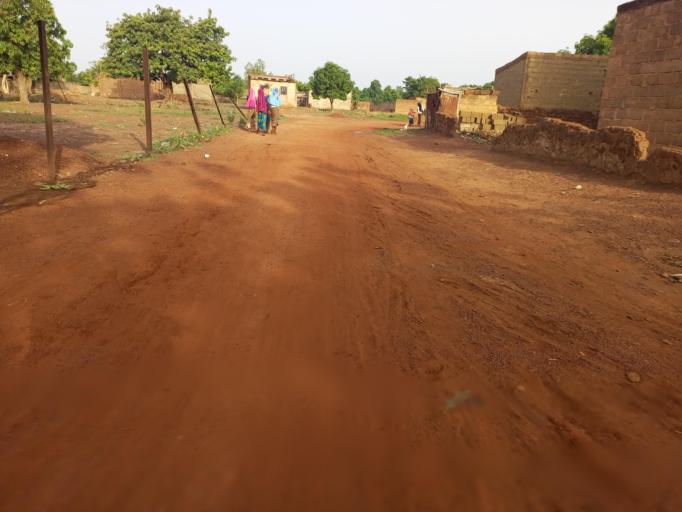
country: ML
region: Bamako
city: Bamako
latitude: 12.5185
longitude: -7.9897
